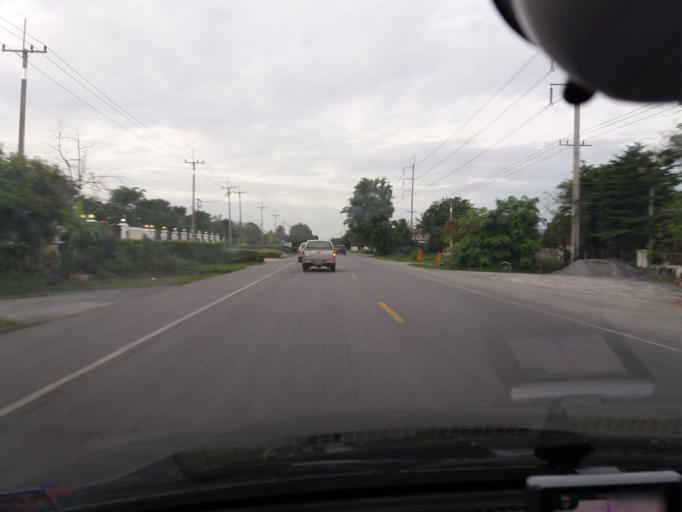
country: TH
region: Suphan Buri
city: U Thong
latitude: 14.5016
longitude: 99.9186
